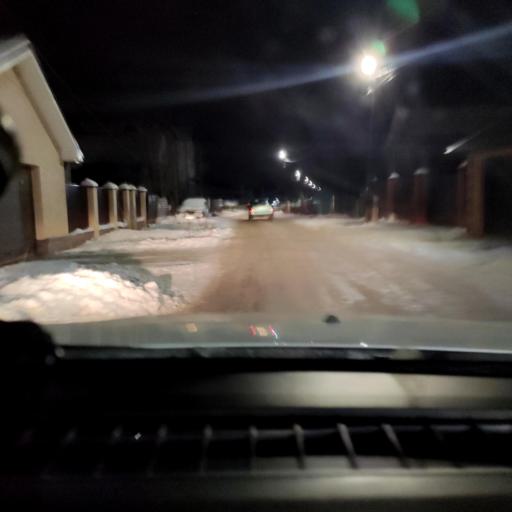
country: RU
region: Samara
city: Samara
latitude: 53.1357
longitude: 50.1010
